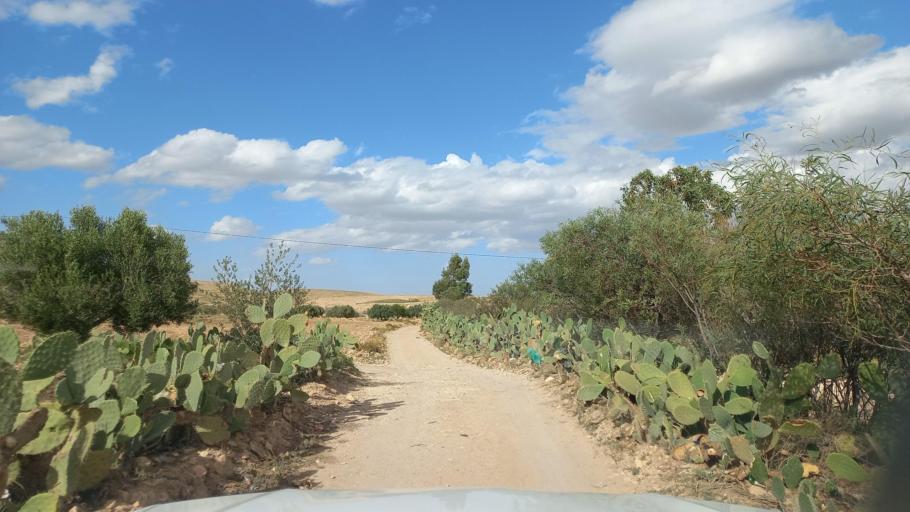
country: TN
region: Al Qasrayn
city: Sbiba
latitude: 35.4513
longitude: 9.0727
